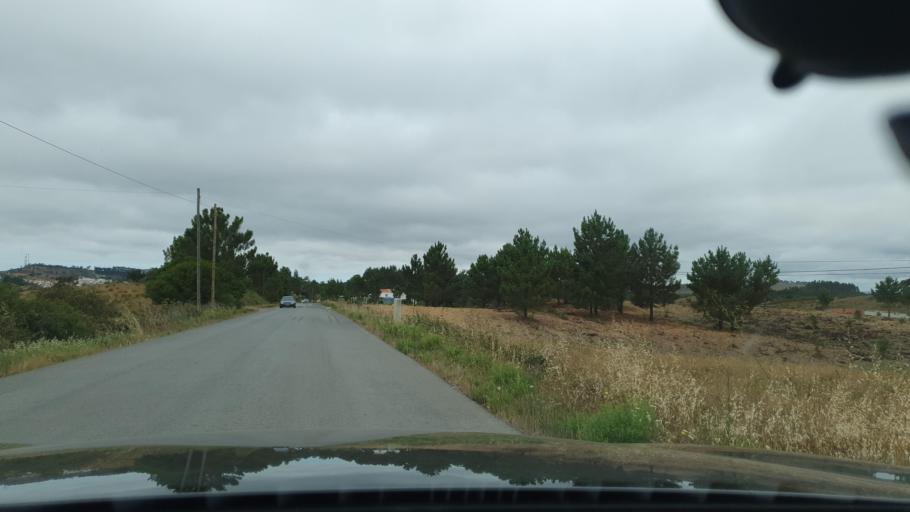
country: PT
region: Beja
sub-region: Odemira
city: Sao Teotonio
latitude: 37.5032
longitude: -8.6898
